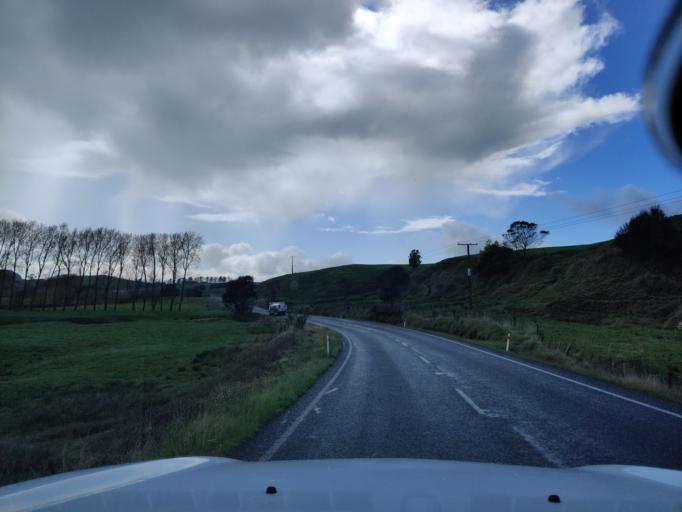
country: NZ
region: Waikato
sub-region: Waikato District
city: Ngaruawahia
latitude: -37.5815
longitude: 175.2186
